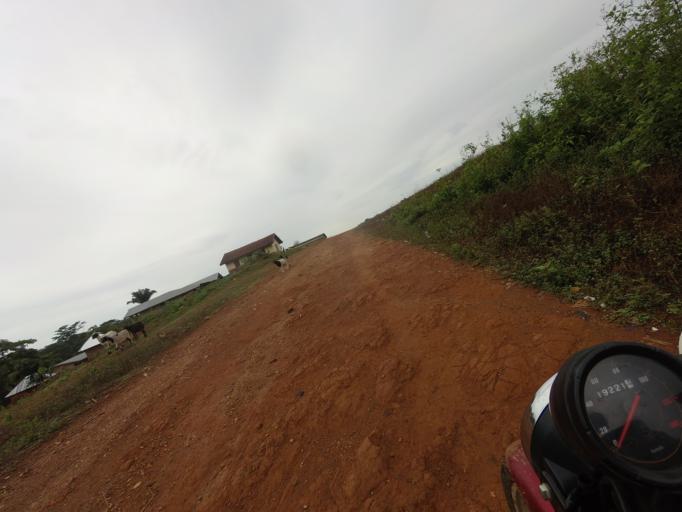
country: LR
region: Nimba
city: New Yekepa
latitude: 7.6519
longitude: -8.5595
